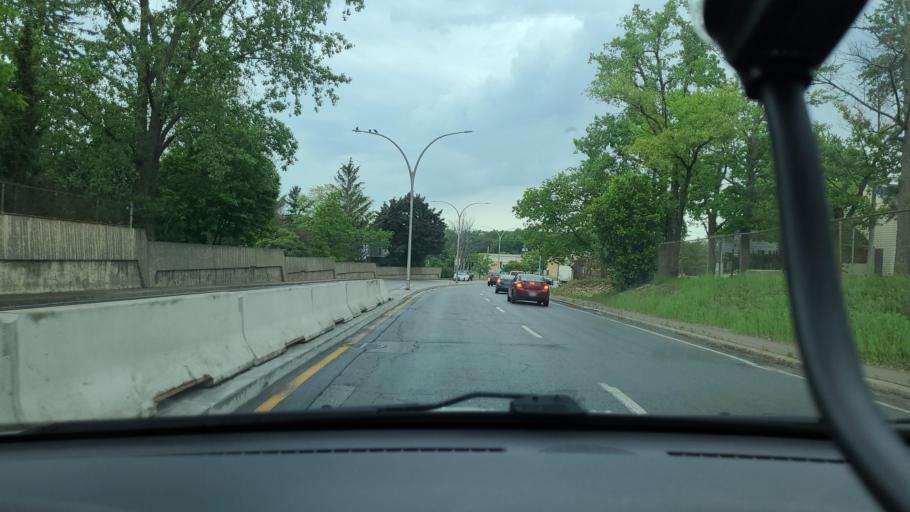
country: CA
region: Quebec
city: Sainte-Anne-de-Bellevue
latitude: 45.4099
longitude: -73.9510
